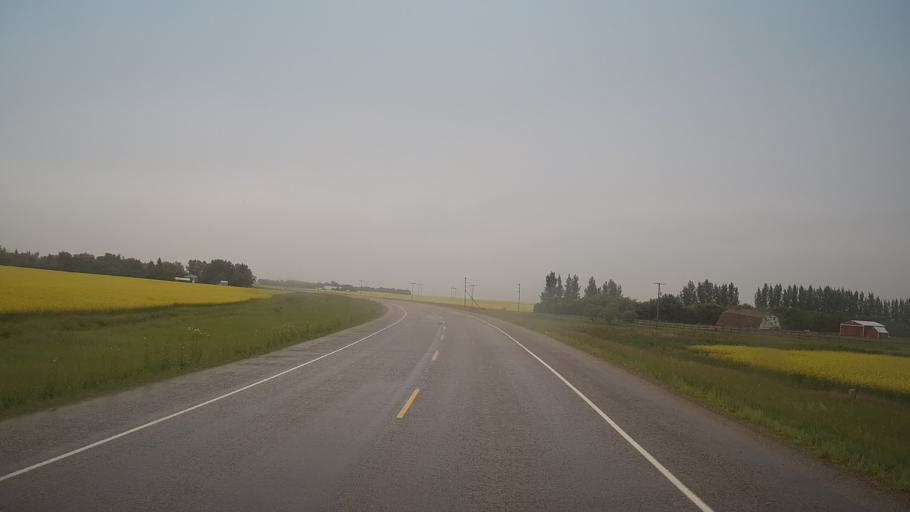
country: CA
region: Saskatchewan
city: Wilkie
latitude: 52.2008
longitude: -108.4407
